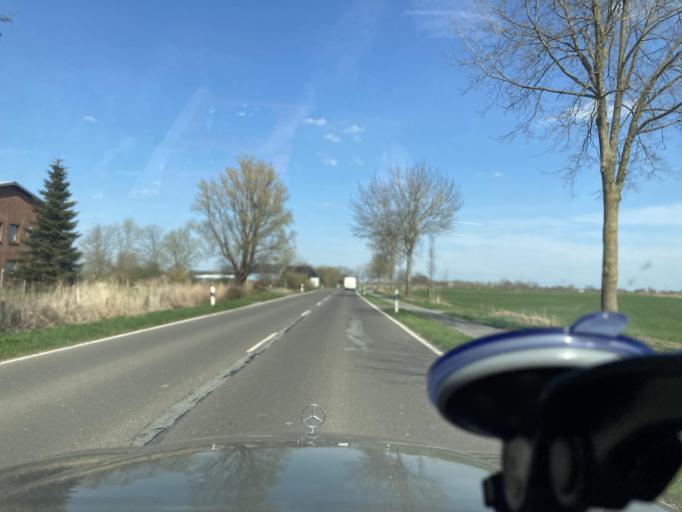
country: DE
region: Schleswig-Holstein
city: Krempel
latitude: 54.3460
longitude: 9.0489
